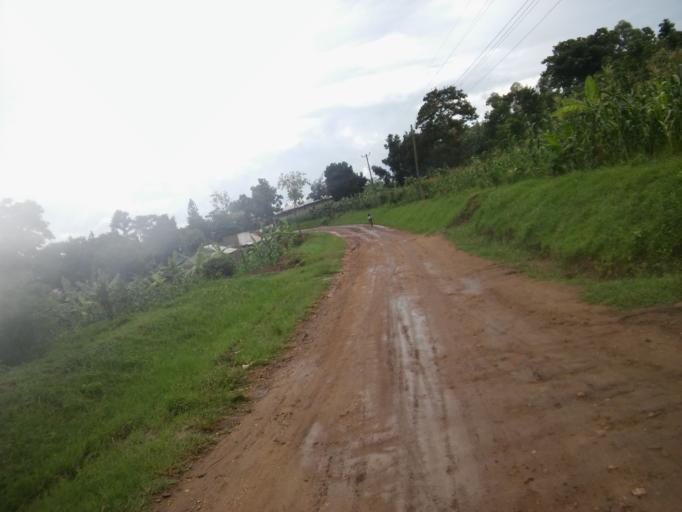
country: UG
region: Eastern Region
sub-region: Mbale District
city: Mbale
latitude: 1.0373
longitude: 34.1945
